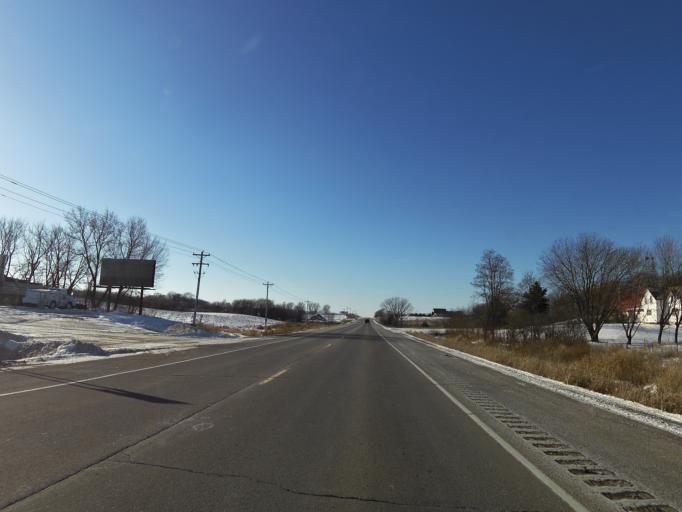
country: US
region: Minnesota
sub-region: Le Sueur County
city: New Prague
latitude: 44.5437
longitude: -93.5120
